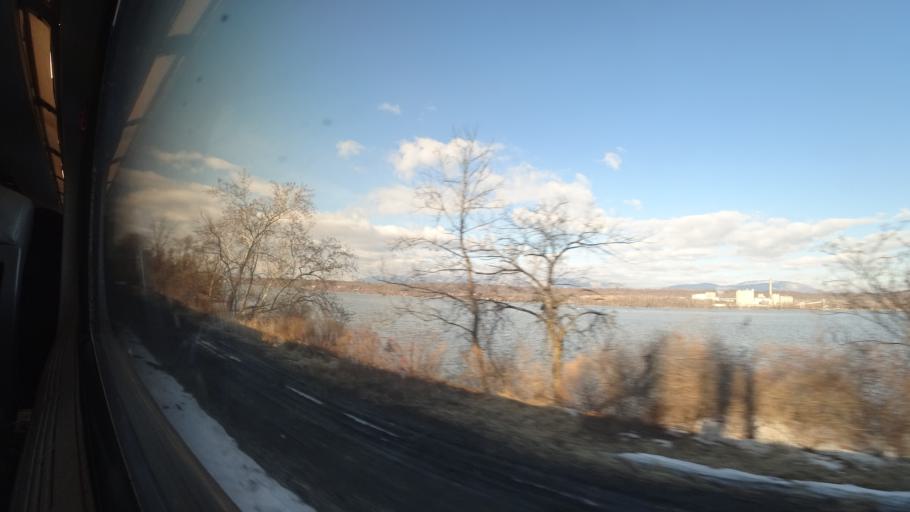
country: US
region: New York
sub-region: Dutchess County
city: Tivoli
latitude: 42.1327
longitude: -73.8990
